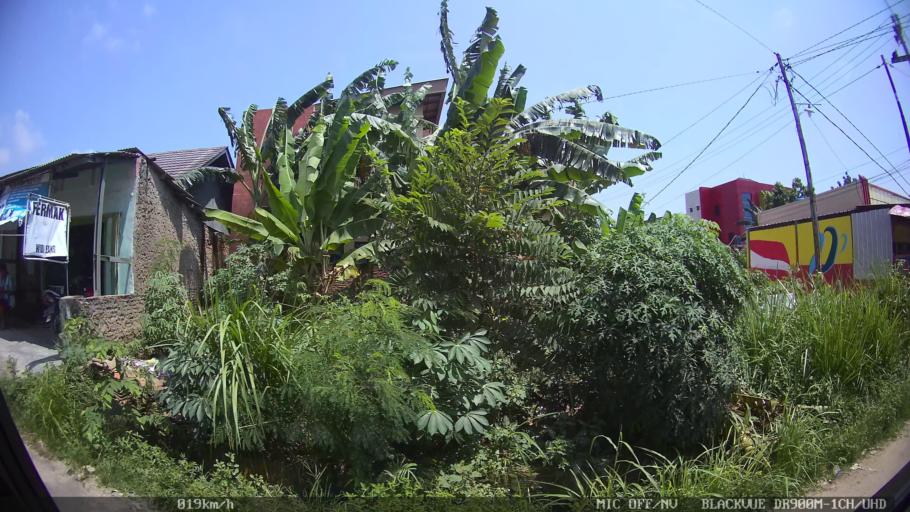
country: ID
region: Lampung
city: Kedaton
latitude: -5.3604
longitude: 105.2729
